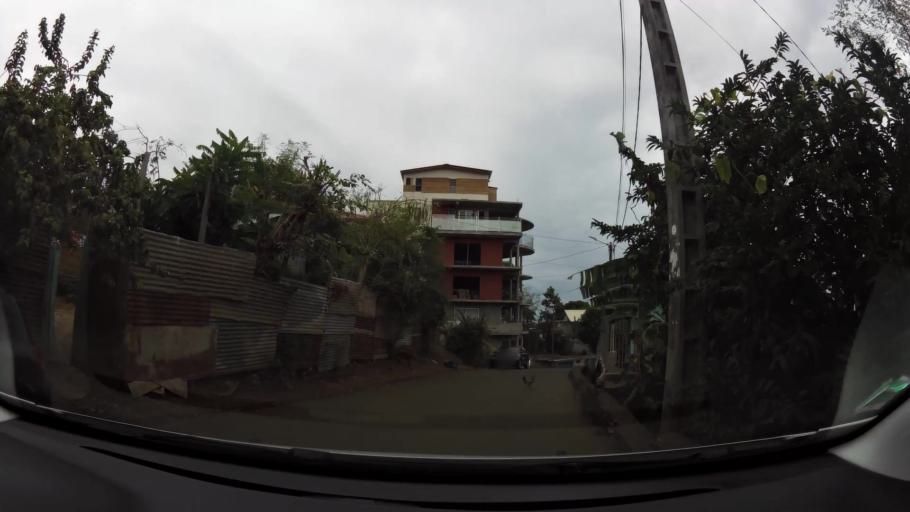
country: YT
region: Sada
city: Sada
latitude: -12.8471
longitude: 45.1043
